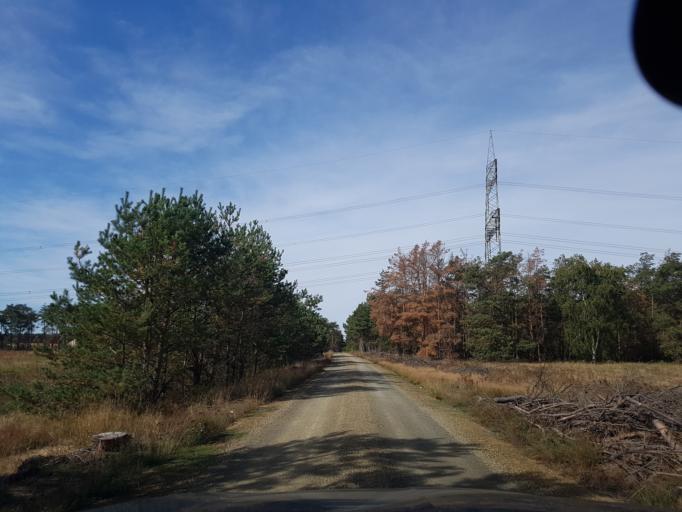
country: DE
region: Brandenburg
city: Schlieben
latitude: 51.6798
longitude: 13.3794
